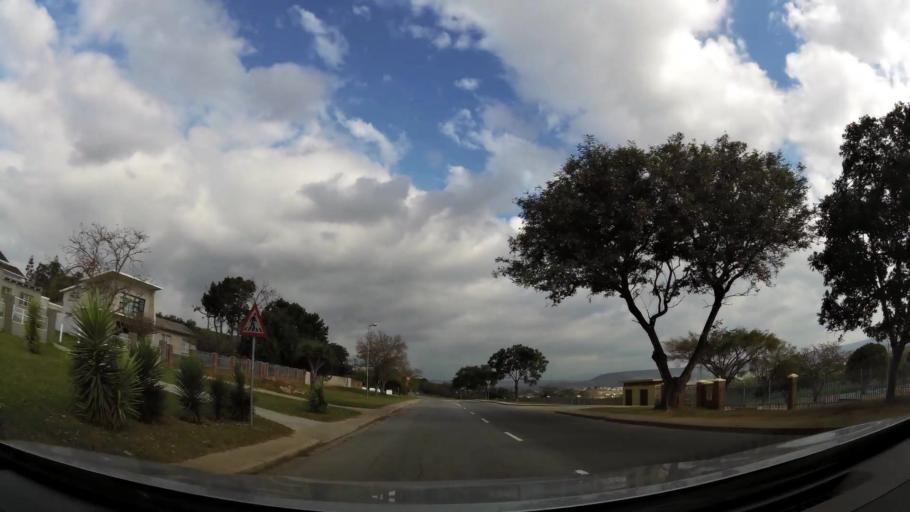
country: ZA
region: Eastern Cape
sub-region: Nelson Mandela Bay Metropolitan Municipality
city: Uitenhage
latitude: -33.7397
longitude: 25.4040
